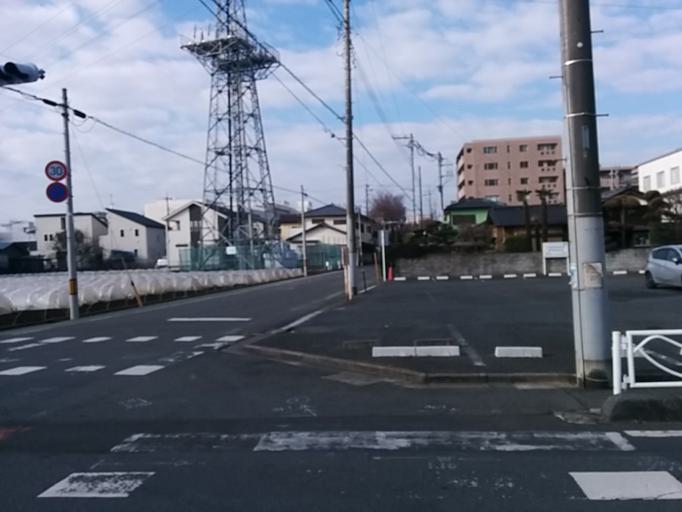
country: JP
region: Saitama
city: Kawagoe
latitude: 35.9058
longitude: 139.4899
